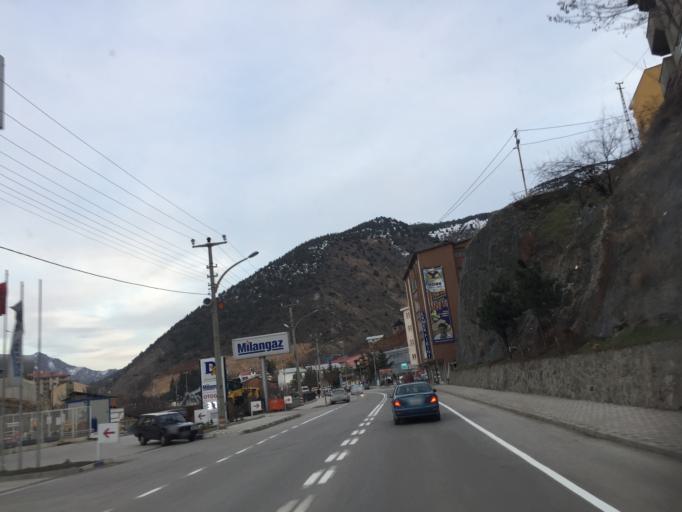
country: TR
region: Gumushane
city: Gumushkhane
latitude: 40.4632
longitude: 39.4656
